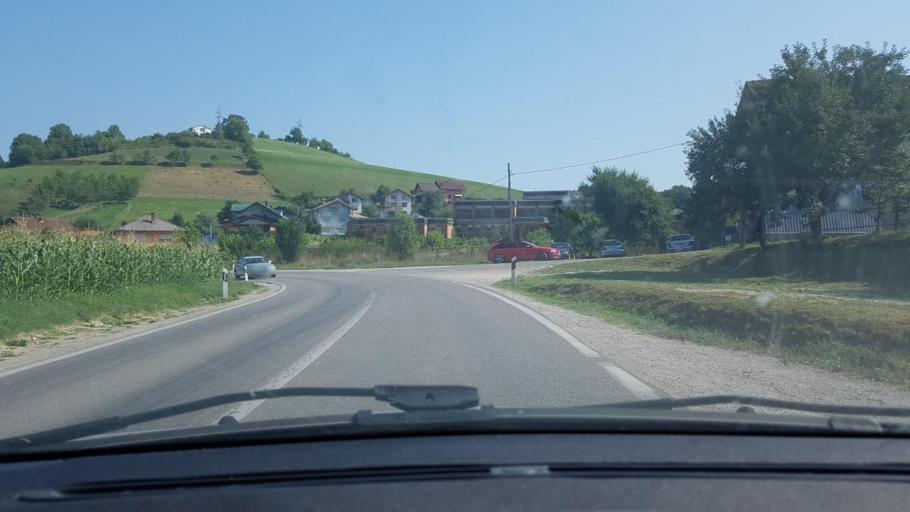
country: BA
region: Federation of Bosnia and Herzegovina
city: Mala Kladusa
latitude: 45.1537
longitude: 15.8293
